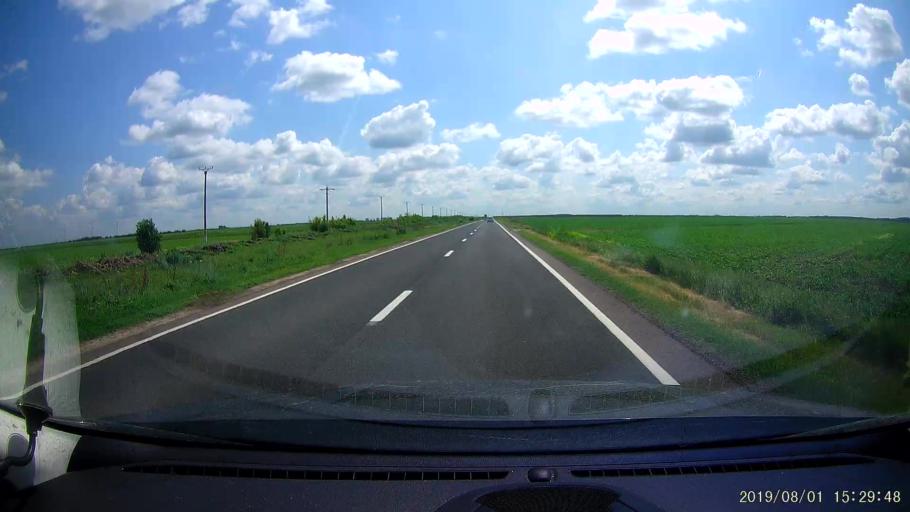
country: RO
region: Braila
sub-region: Comuna Viziru
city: Viziru
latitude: 44.9750
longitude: 27.6895
